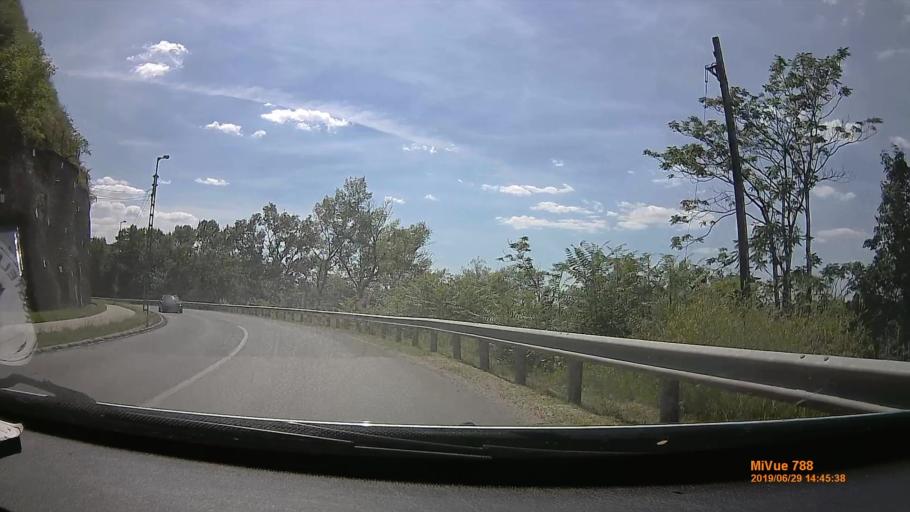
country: HU
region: Komarom-Esztergom
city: Nyergesujfalu
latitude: 47.7610
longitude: 18.5366
